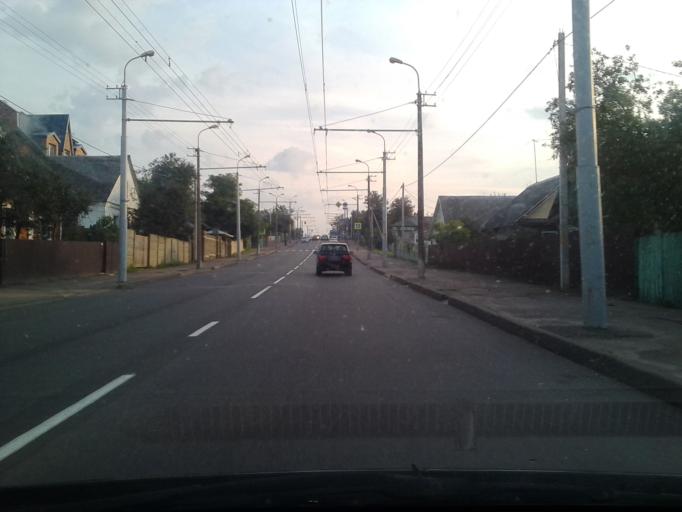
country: BY
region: Minsk
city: Minsk
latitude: 53.9444
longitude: 27.5906
